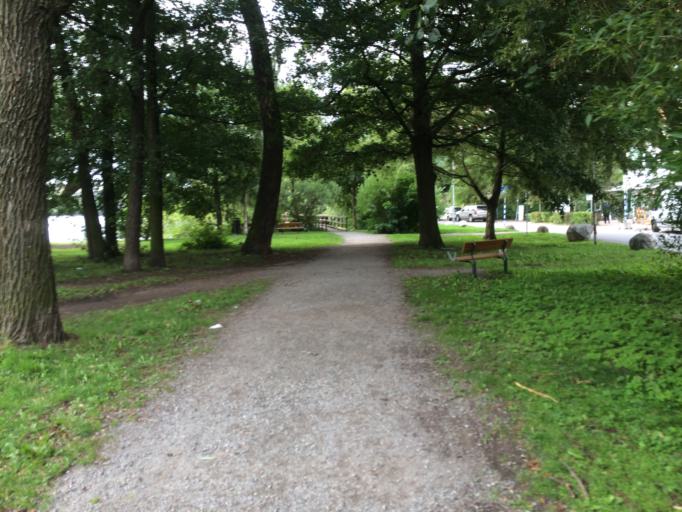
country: SE
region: Stockholm
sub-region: Solna Kommun
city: Solna
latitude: 59.3317
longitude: 17.9852
